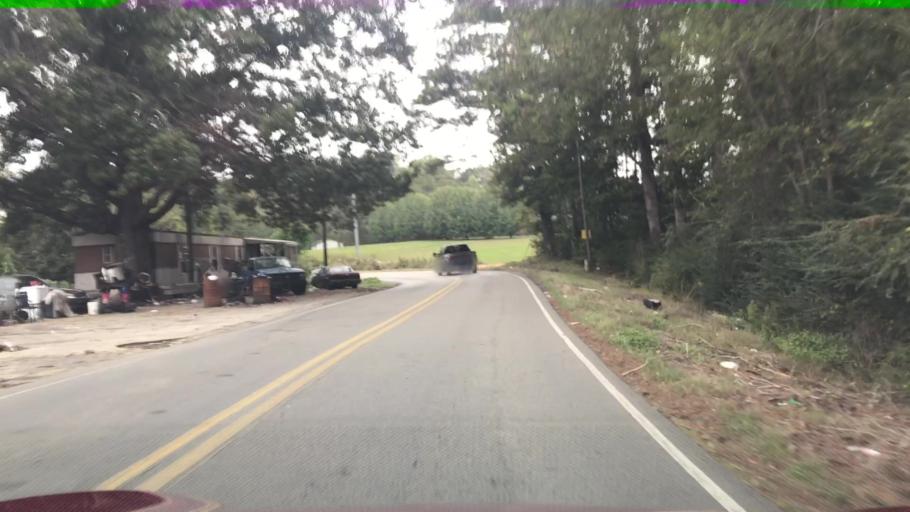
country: US
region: Alabama
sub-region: Cullman County
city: Good Hope
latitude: 34.0962
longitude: -87.0563
